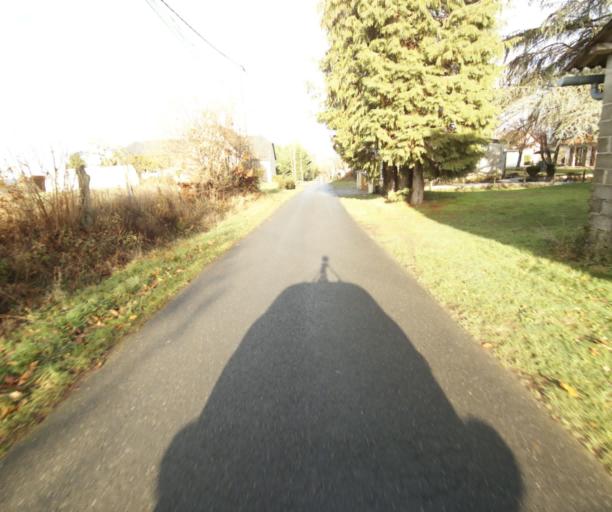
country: FR
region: Limousin
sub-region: Departement de la Correze
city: Saint-Mexant
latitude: 45.2536
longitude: 1.6275
